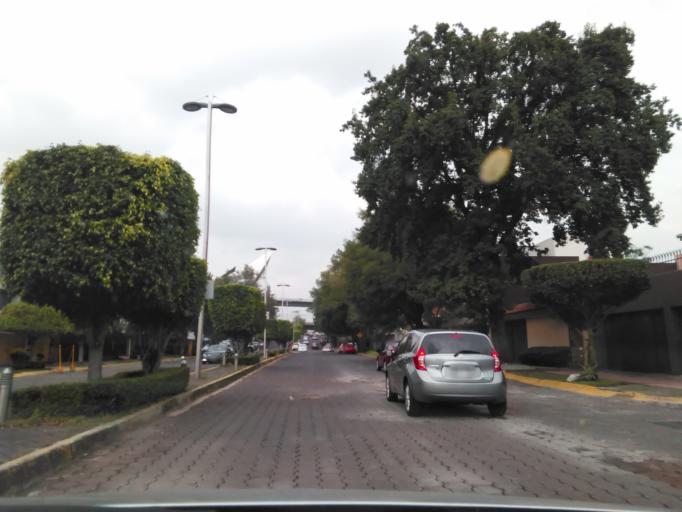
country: MX
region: Mexico City
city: Tlalpan
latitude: 19.2990
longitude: -99.1925
